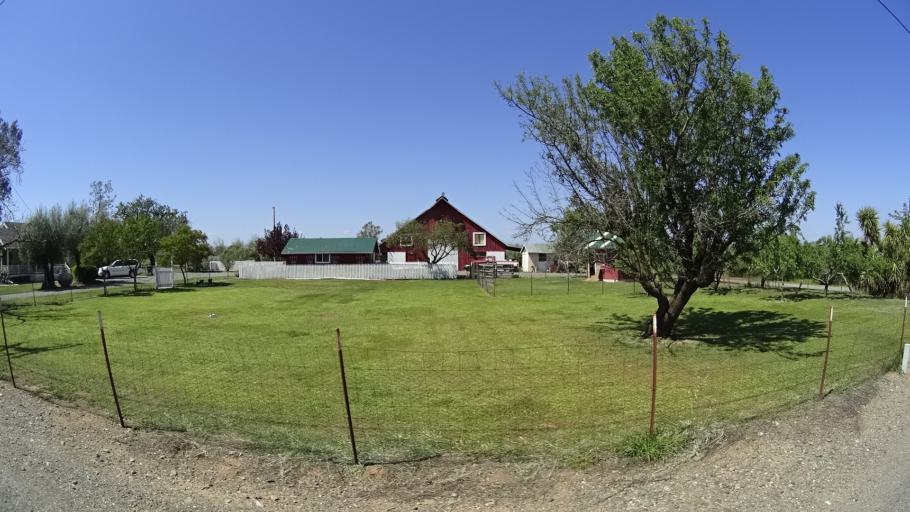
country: US
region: California
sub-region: Glenn County
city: Orland
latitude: 39.7733
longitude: -122.1783
